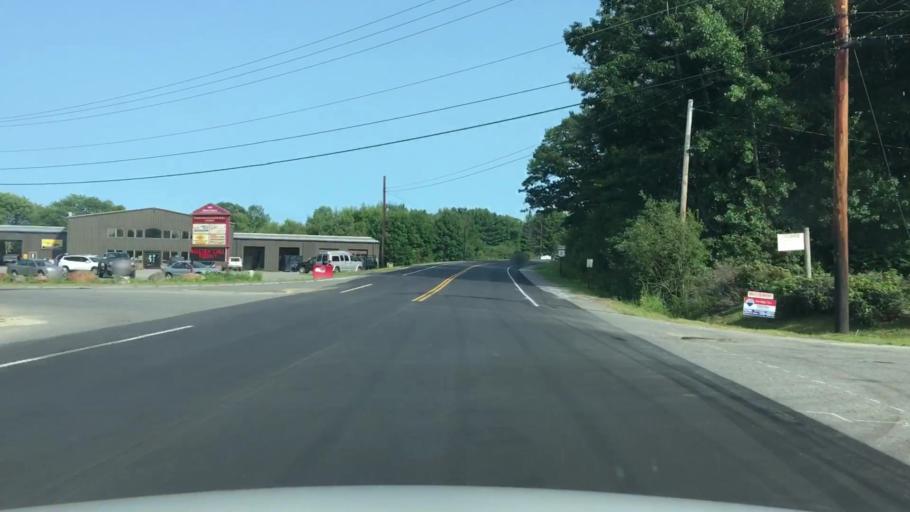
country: US
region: Maine
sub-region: Knox County
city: Warren
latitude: 44.1149
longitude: -69.2585
